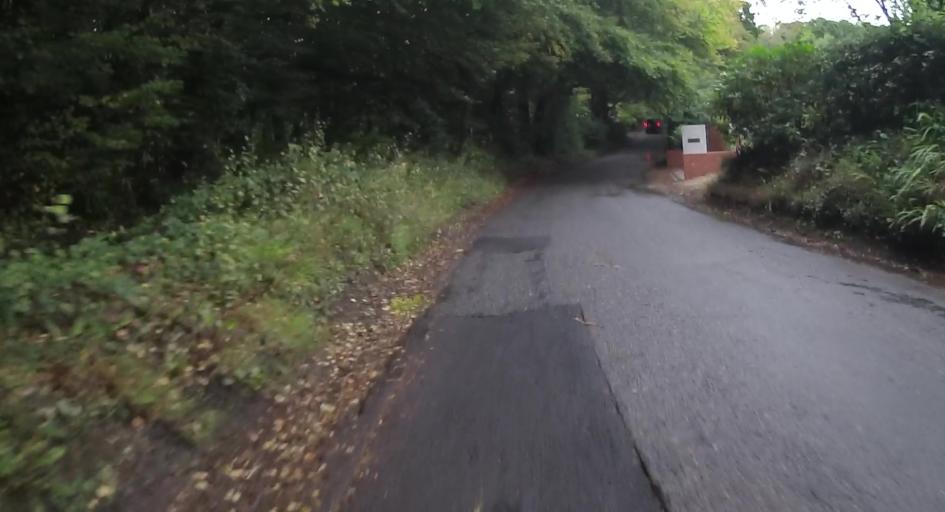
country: GB
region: England
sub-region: West Berkshire
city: Thatcham
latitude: 51.4199
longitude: -1.1799
